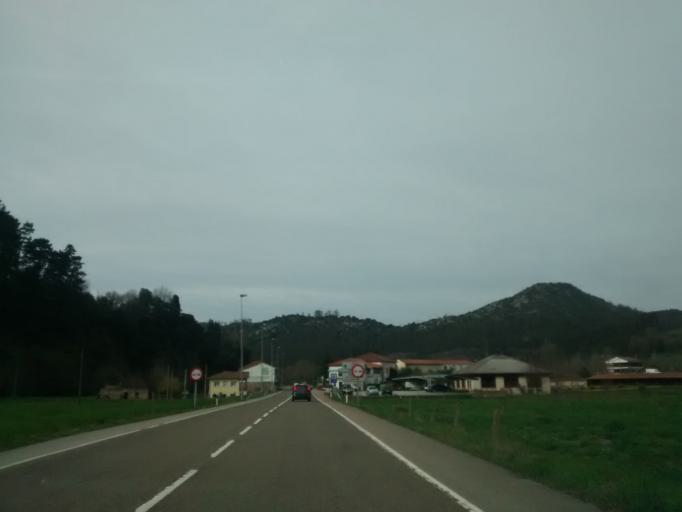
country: ES
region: Cantabria
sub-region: Provincia de Cantabria
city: Corvera
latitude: 43.2747
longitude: -3.9471
